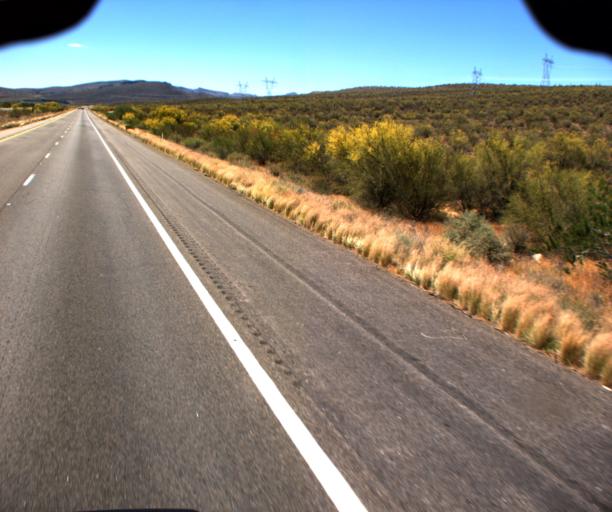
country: US
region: Arizona
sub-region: Yavapai County
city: Bagdad
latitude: 34.5199
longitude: -113.4224
